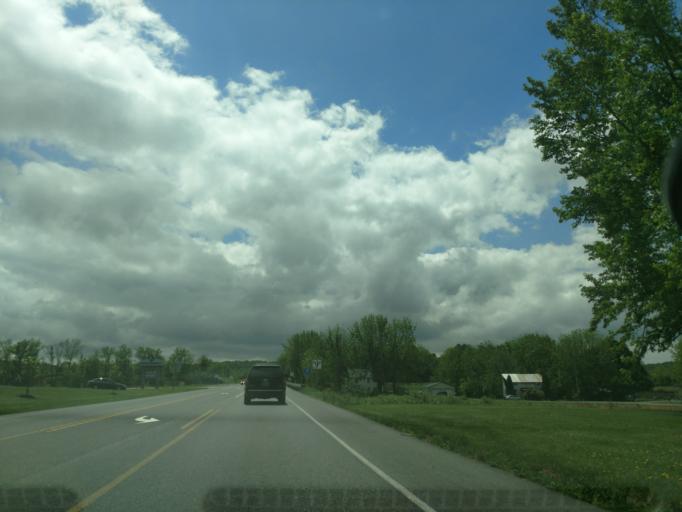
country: US
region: Pennsylvania
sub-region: Lebanon County
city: Cornwall
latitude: 40.2769
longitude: -76.4357
